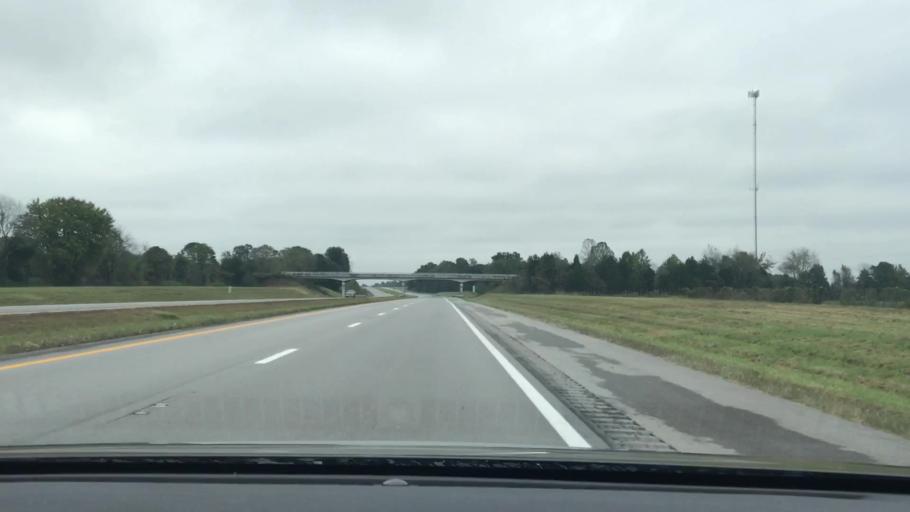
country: US
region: Kentucky
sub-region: Russell County
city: Russell Springs
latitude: 37.0547
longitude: -85.1666
